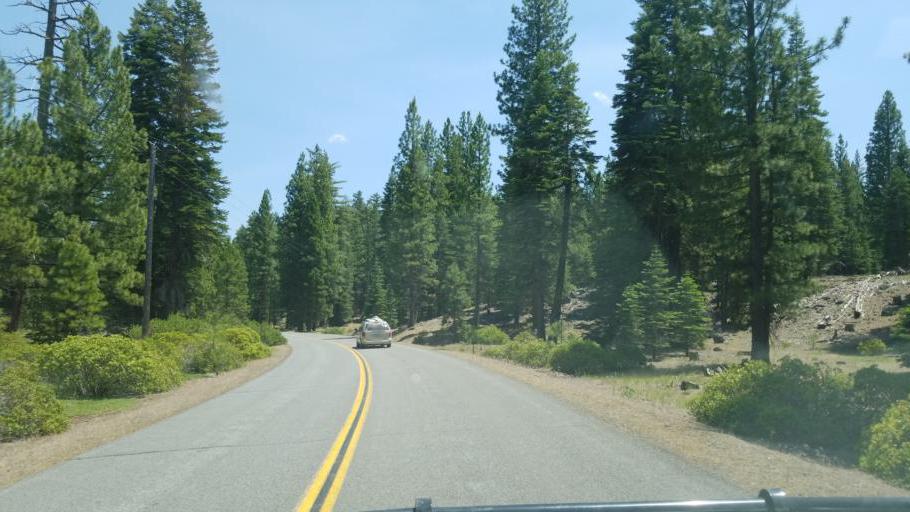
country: US
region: California
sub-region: Lassen County
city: Susanville
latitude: 40.5629
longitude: -120.8364
